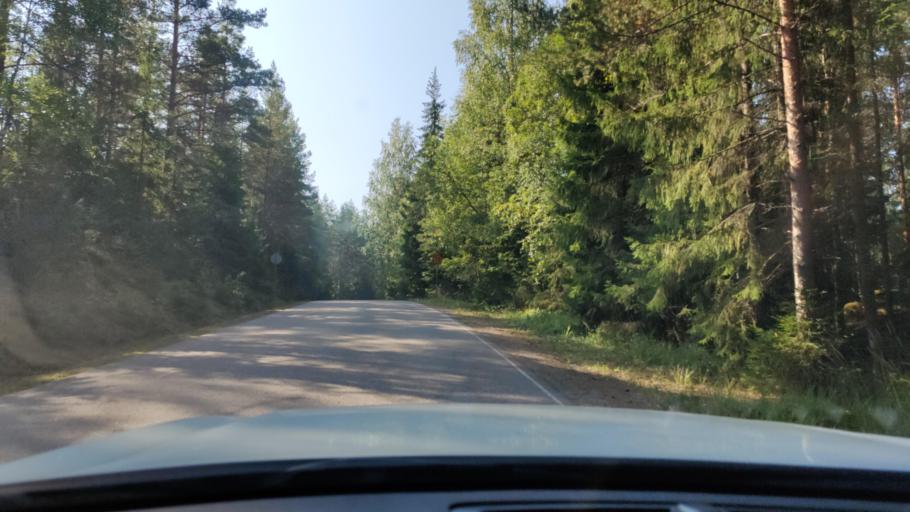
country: FI
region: Haeme
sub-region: Riihimaeki
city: Riihimaeki
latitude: 60.7055
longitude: 24.6868
